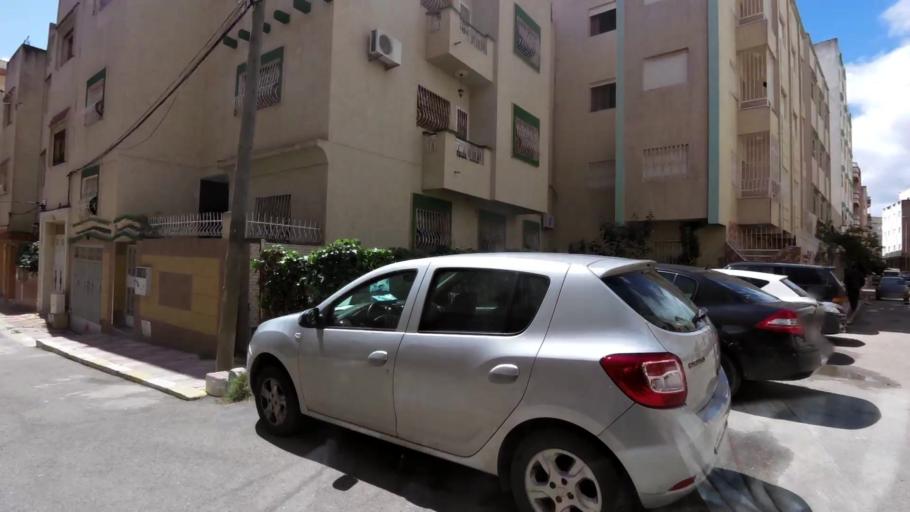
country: MA
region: Tanger-Tetouan
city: Tetouan
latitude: 35.5771
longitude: -5.3422
